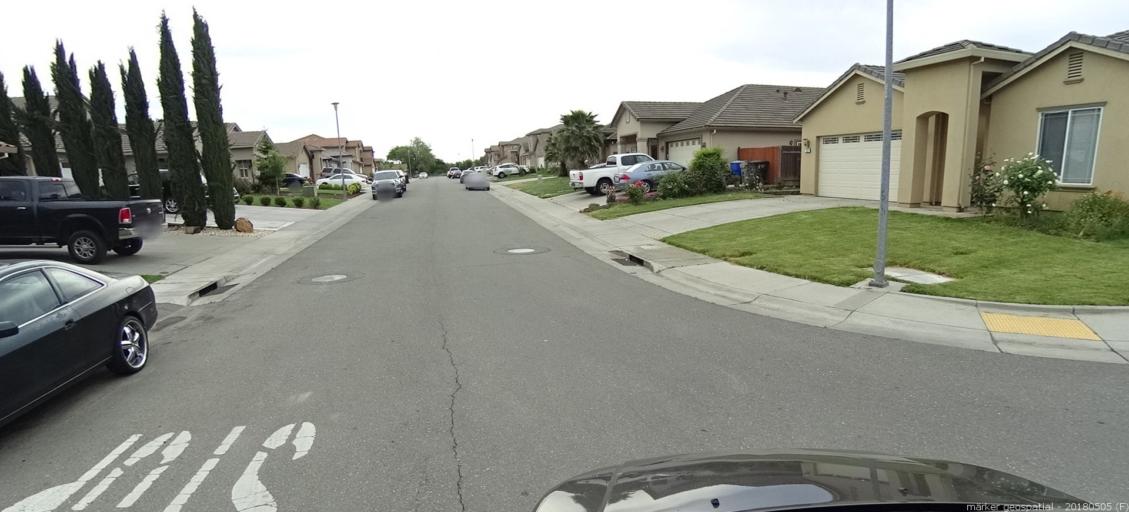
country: US
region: California
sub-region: Sacramento County
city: Rio Linda
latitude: 38.6630
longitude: -121.4451
